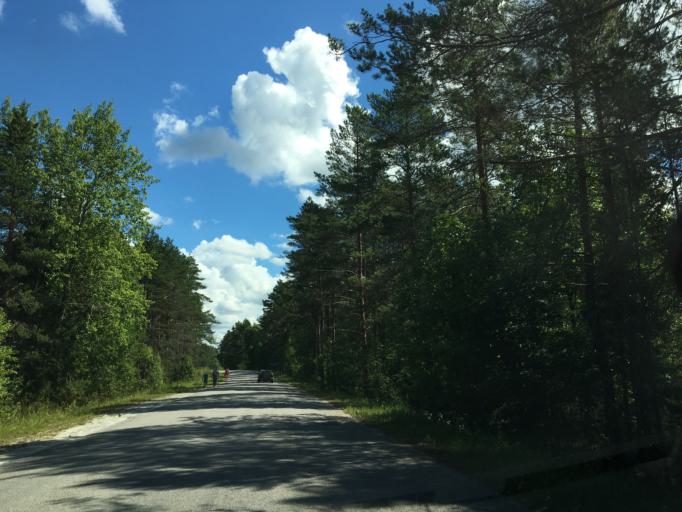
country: EE
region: Harju
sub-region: Nissi vald
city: Riisipere
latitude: 59.2435
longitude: 24.2831
